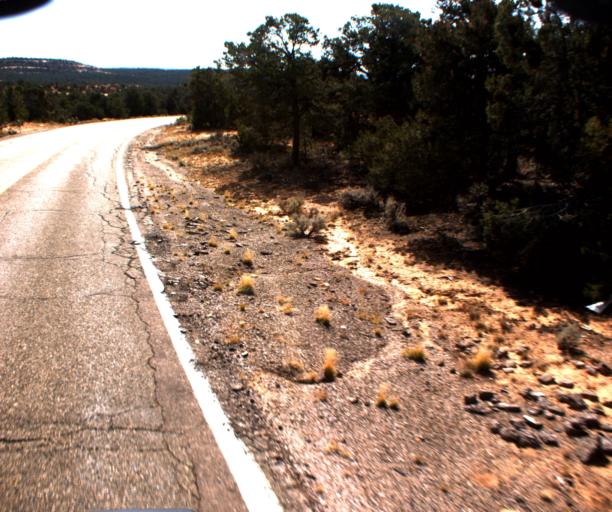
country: US
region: Arizona
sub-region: Navajo County
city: Kayenta
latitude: 36.6645
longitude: -110.5275
